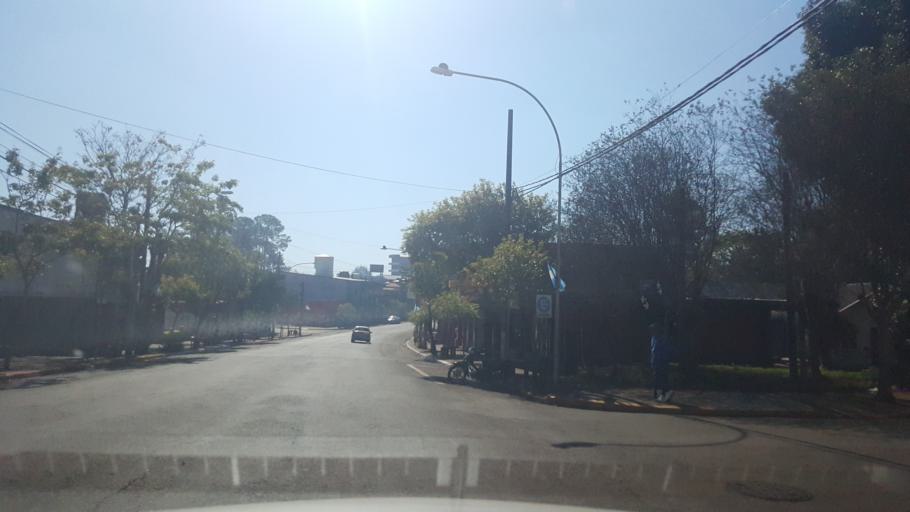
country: AR
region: Misiones
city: Puerto Rico
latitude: -26.8151
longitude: -55.0264
